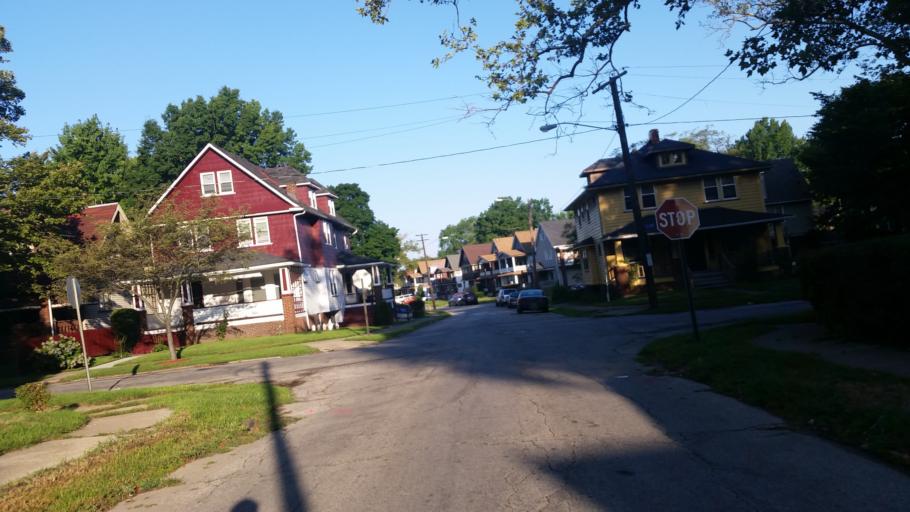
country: US
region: Ohio
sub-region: Cuyahoga County
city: East Cleveland
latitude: 41.5473
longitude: -81.5814
